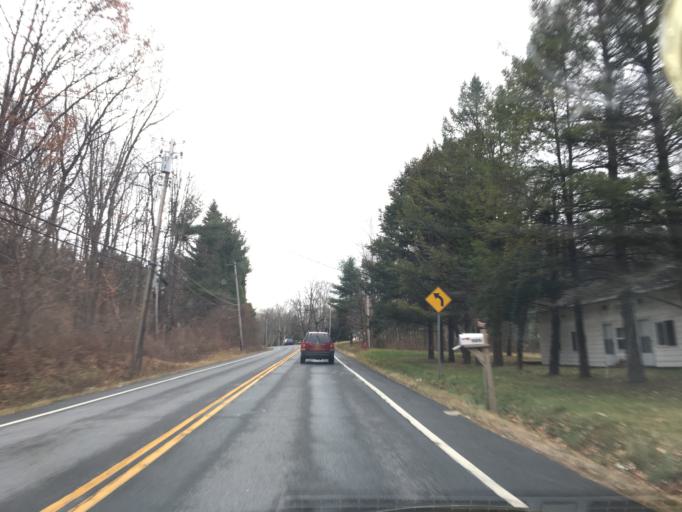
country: US
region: New York
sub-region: Rensselaer County
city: West Sand Lake
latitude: 42.6821
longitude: -73.6059
